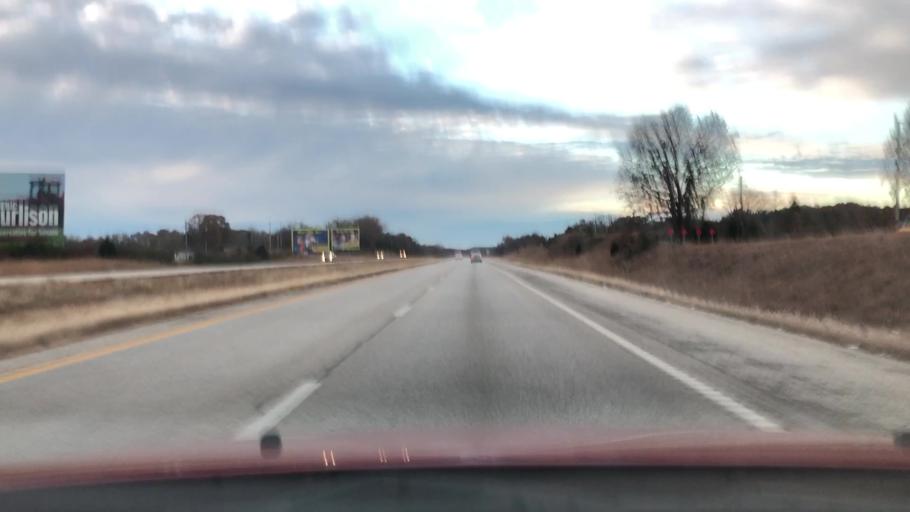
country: US
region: Missouri
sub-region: Christian County
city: Ozark
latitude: 36.9380
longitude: -93.2323
